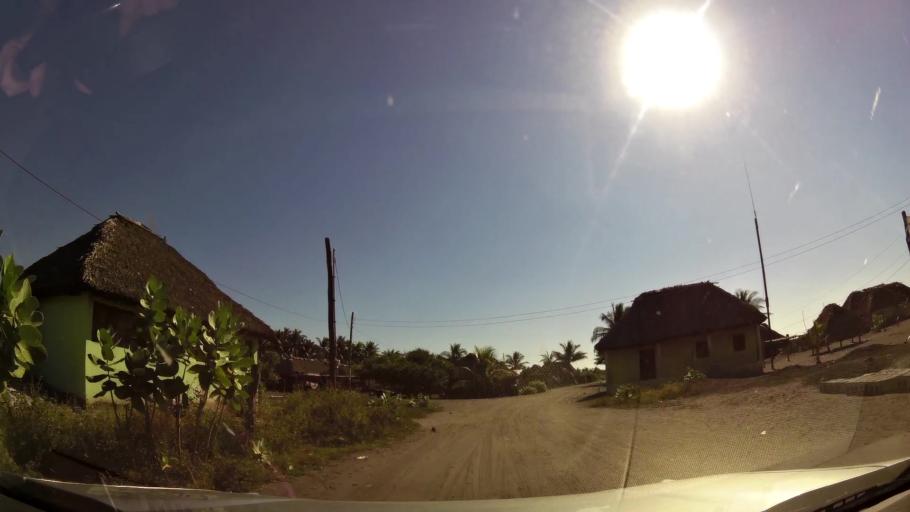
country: GT
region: Jutiapa
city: Pasaco
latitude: 13.8554
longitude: -90.3869
